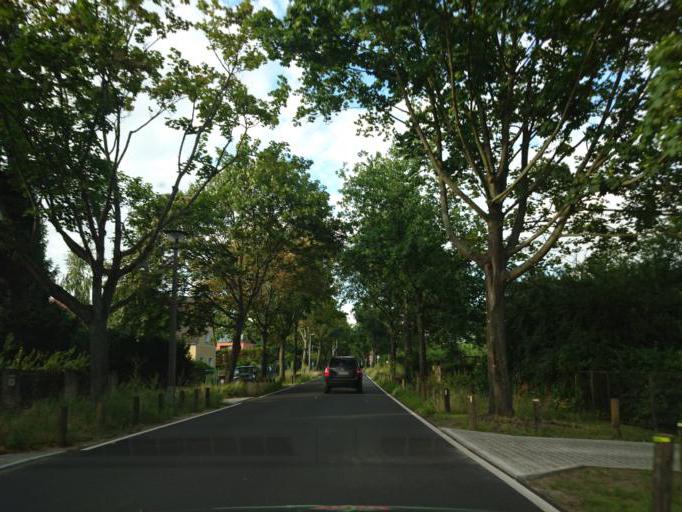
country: DE
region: Berlin
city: Baumschulenweg
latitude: 52.4490
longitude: 13.4857
